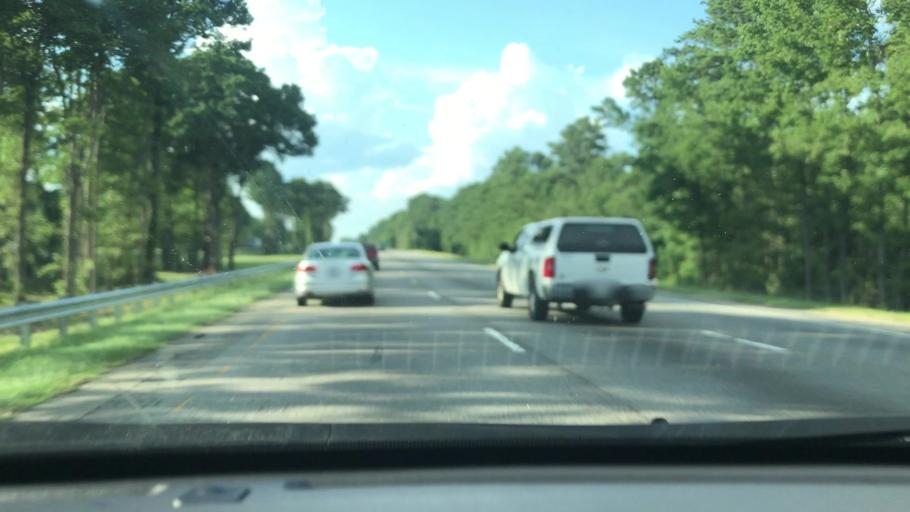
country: US
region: North Carolina
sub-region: Robeson County
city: Lumberton
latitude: 34.7089
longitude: -78.9975
